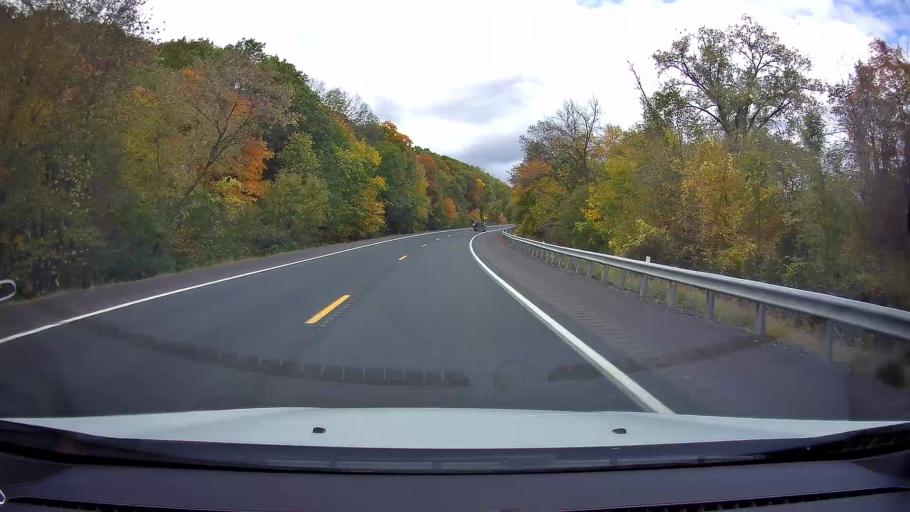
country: US
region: Wisconsin
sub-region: Polk County
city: Saint Croix Falls
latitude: 45.4122
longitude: -92.6539
